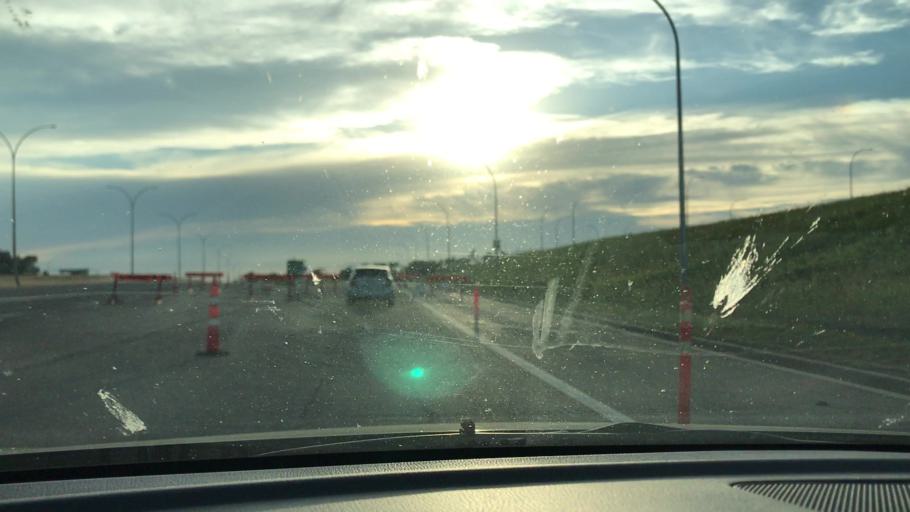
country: CA
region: Alberta
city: Edmonton
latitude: 53.4821
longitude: -113.5082
